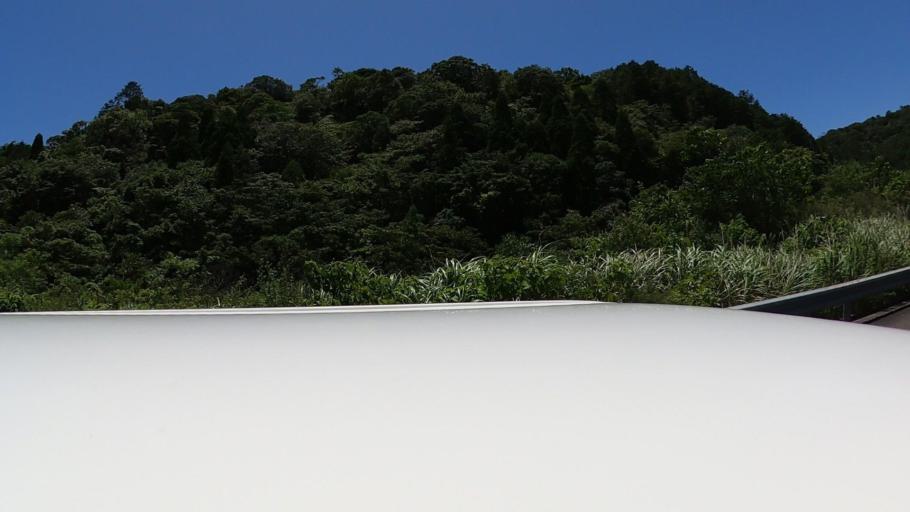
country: JP
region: Miyazaki
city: Nobeoka
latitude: 32.5390
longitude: 131.6582
